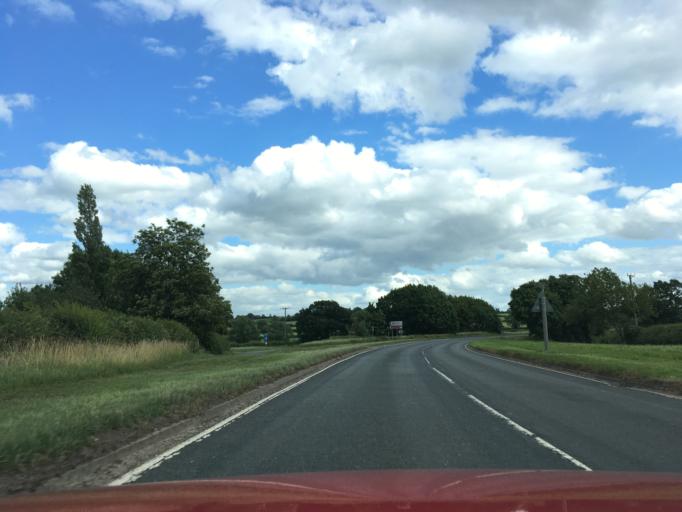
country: GB
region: England
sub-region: Warwickshire
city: Atherstone
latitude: 52.6266
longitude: -1.4842
